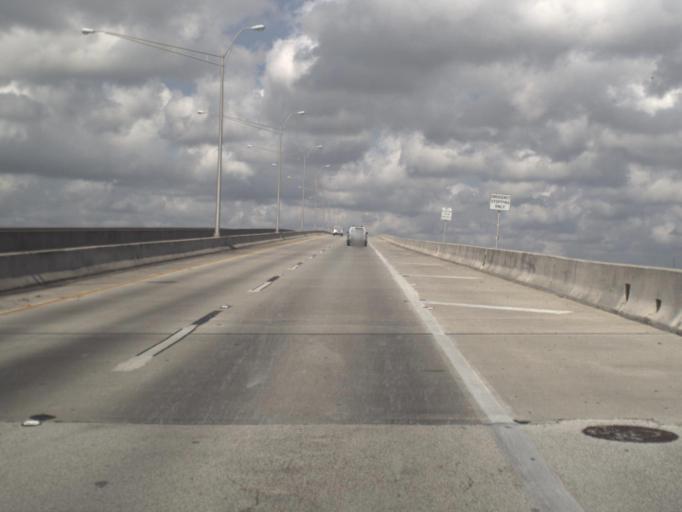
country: US
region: Florida
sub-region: Saint Johns County
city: Saint Augustine South
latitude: 29.8673
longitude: -81.3026
